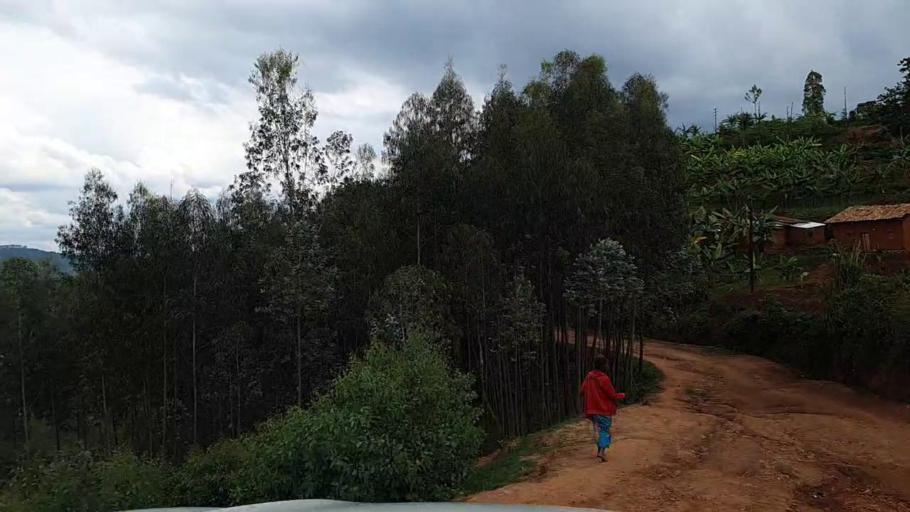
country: RW
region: Southern Province
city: Gikongoro
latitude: -2.4213
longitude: 29.6499
